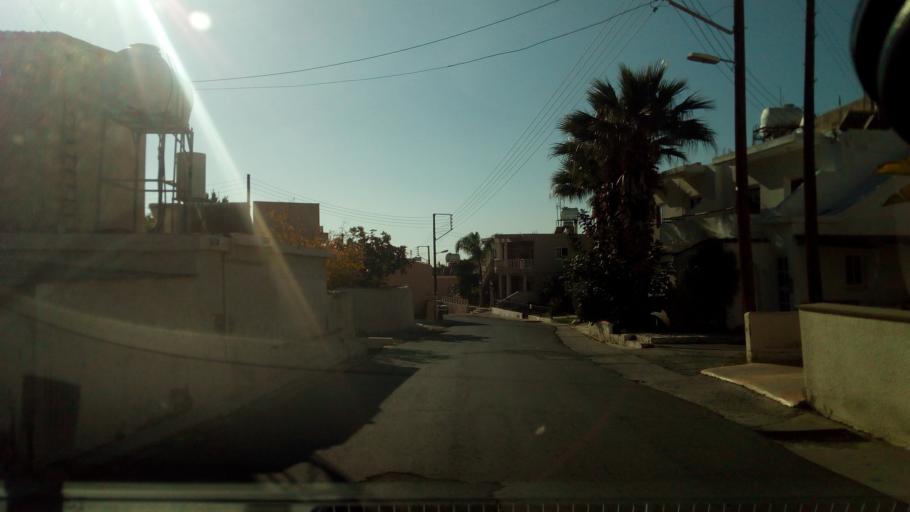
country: CY
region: Larnaka
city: Voroklini
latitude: 34.9879
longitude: 33.6524
